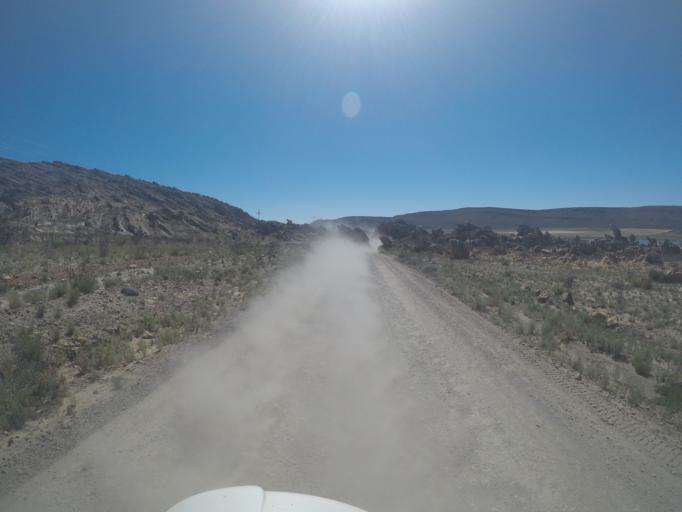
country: ZA
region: Western Cape
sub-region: Cape Winelands District Municipality
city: Ceres
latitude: -32.8484
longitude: 19.4458
